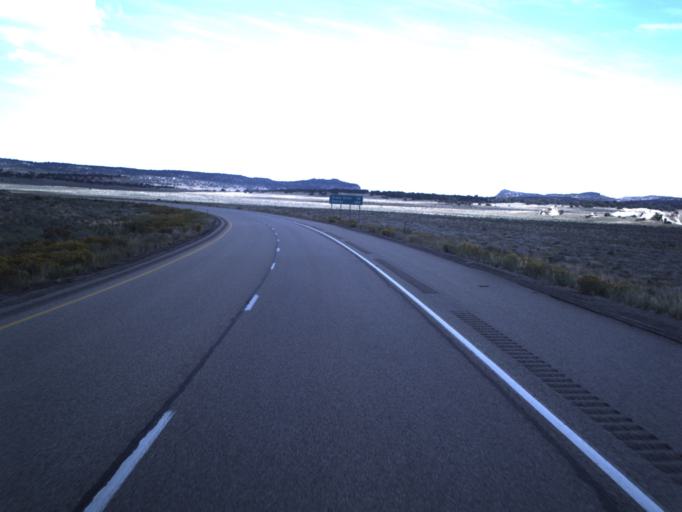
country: US
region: Utah
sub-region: Emery County
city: Ferron
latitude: 38.8648
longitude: -110.7983
